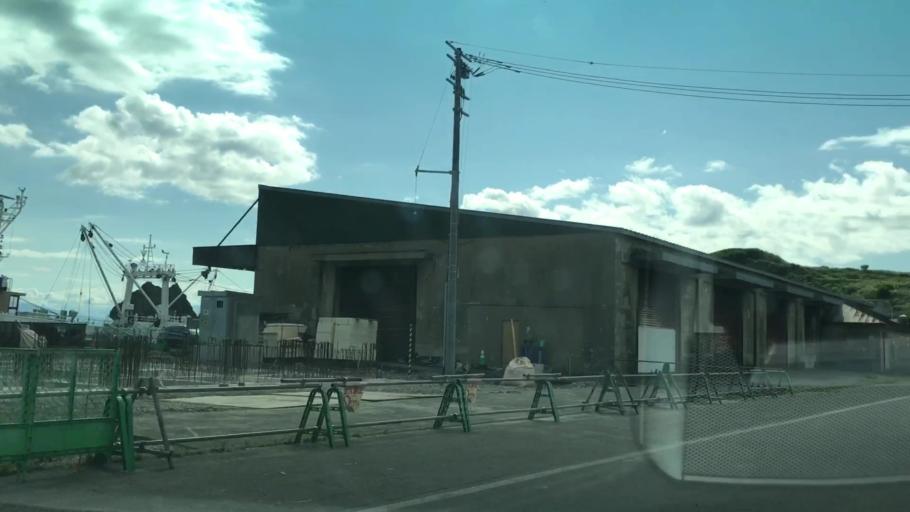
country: JP
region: Hokkaido
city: Muroran
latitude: 42.3092
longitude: 140.9730
